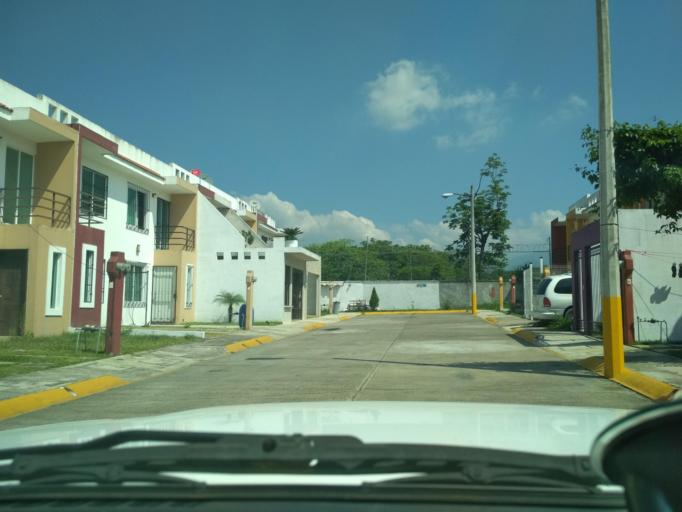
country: MX
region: Veracruz
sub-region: Fortin
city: Fraccionamiento Villas de la Llave
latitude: 18.9149
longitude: -96.9860
